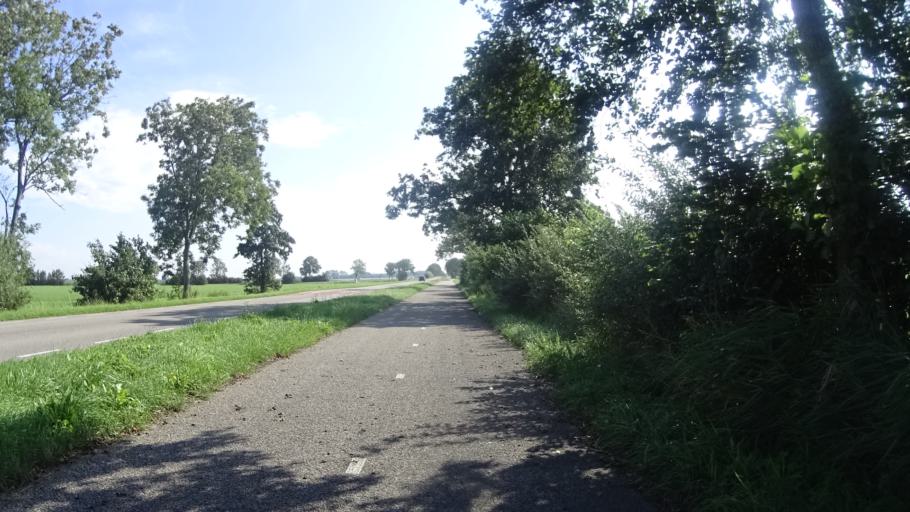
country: NL
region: Friesland
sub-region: Menameradiel
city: Dronryp
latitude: 53.1966
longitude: 5.6229
